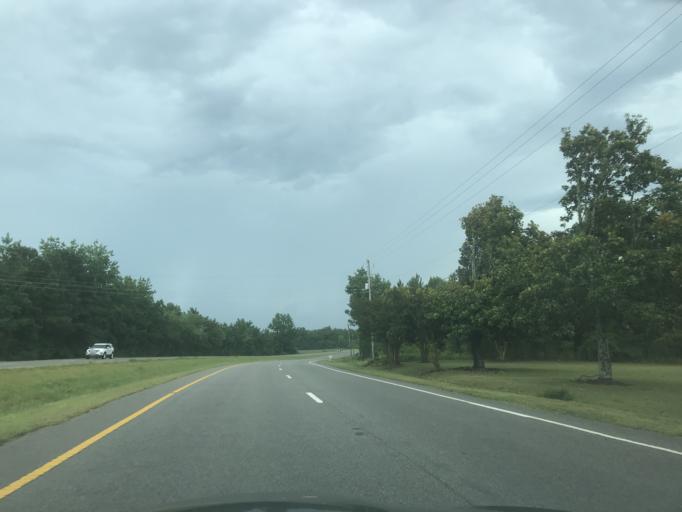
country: US
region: North Carolina
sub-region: Johnston County
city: Wilsons Mills
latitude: 35.5715
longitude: -78.3949
